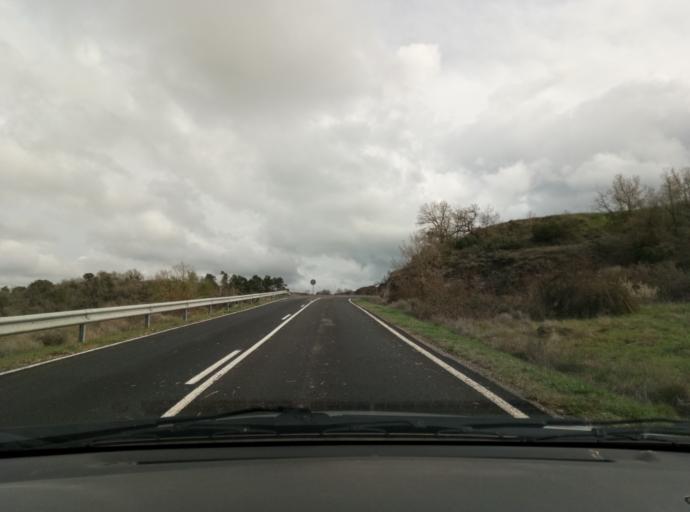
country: ES
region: Catalonia
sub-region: Provincia de Tarragona
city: Santa Coloma de Queralt
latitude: 41.5756
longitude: 1.3367
